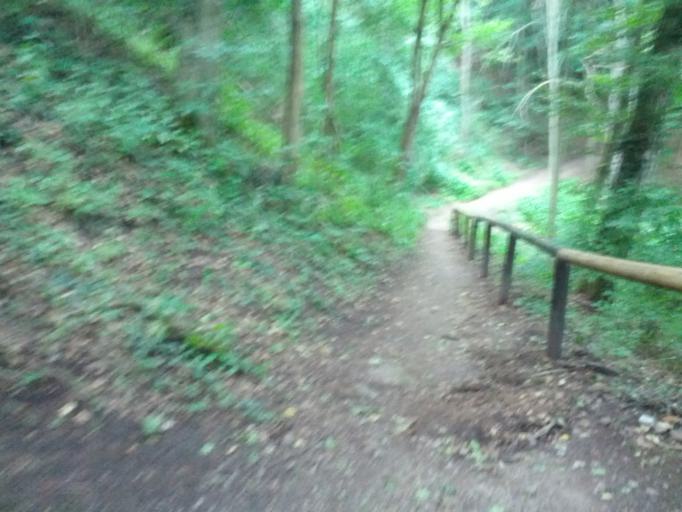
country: DE
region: Thuringia
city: Eisenach
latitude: 50.9653
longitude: 10.3076
